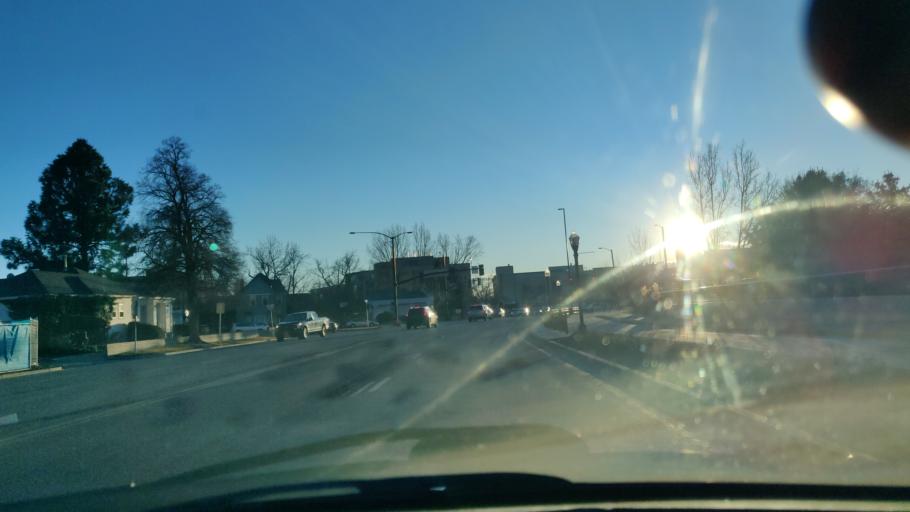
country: US
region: Idaho
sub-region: Ada County
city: Boise
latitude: 43.6118
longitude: -116.1918
